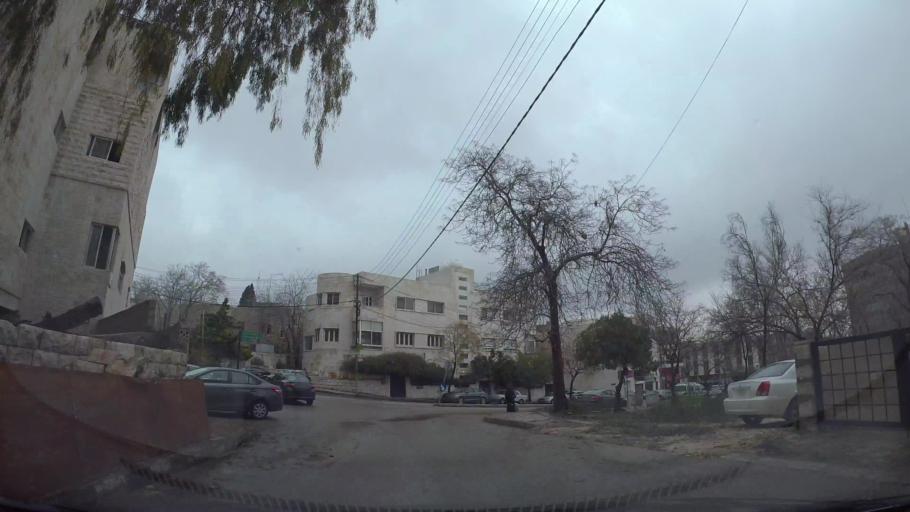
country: JO
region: Amman
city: Amman
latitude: 31.9495
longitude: 35.9226
